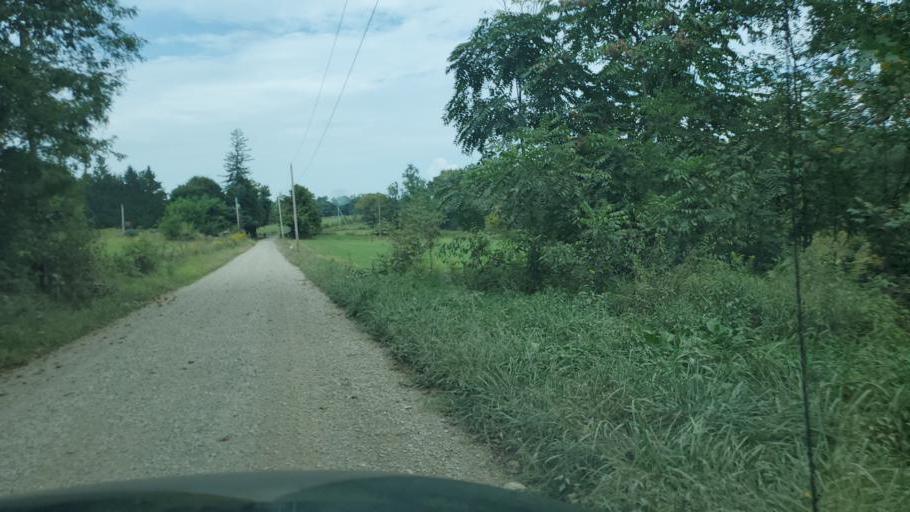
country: US
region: Ohio
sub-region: Muskingum County
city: Frazeysburg
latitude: 39.9723
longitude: -82.2125
